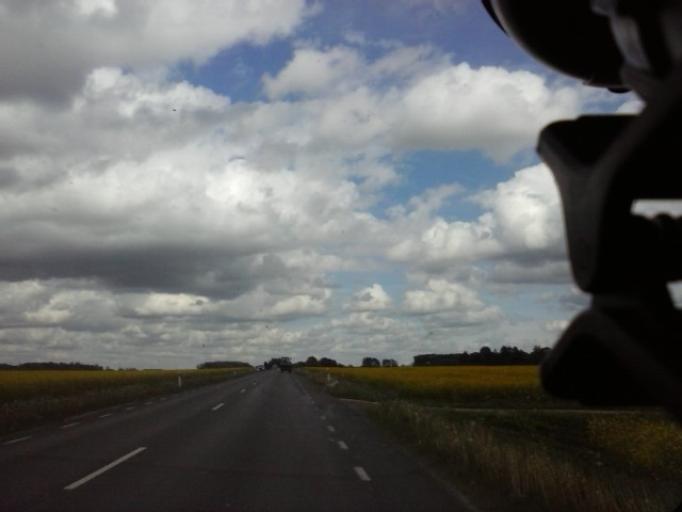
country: EE
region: Jogevamaa
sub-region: Poltsamaa linn
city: Poltsamaa
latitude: 58.6345
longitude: 25.8150
